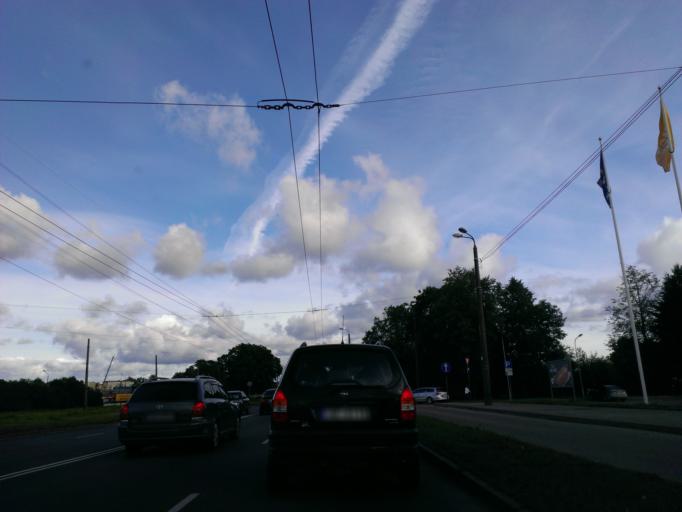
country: LV
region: Stopini
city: Ulbroka
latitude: 56.9587
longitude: 24.2335
